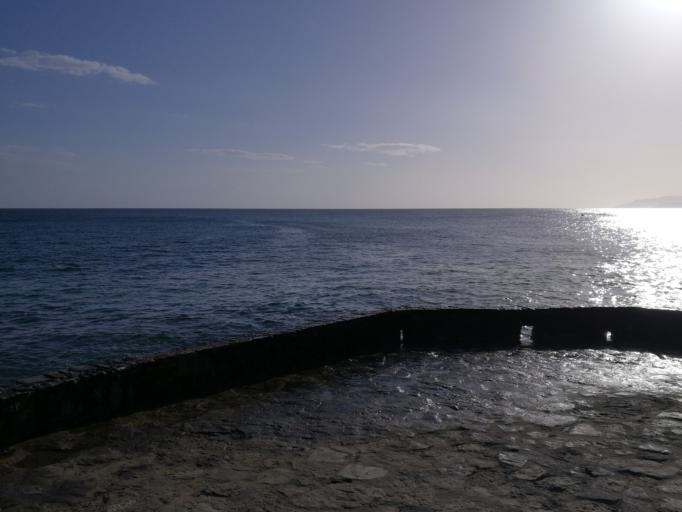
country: GR
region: Crete
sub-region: Nomos Irakleiou
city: Stalis
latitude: 35.3048
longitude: 25.4218
